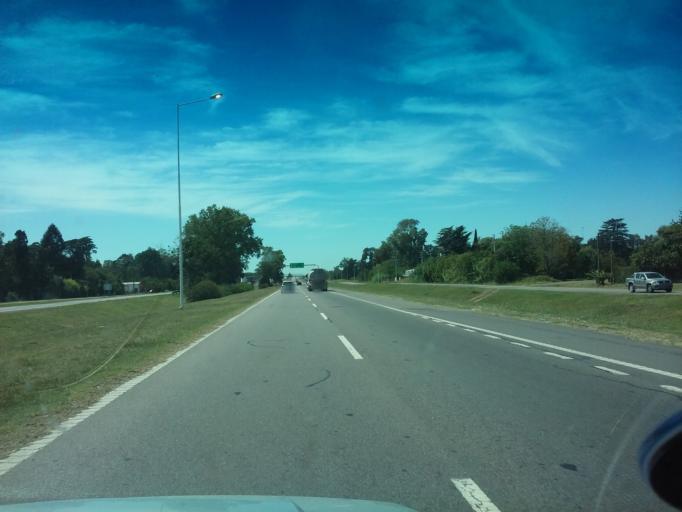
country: AR
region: Buenos Aires
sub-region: Partido de Mercedes
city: Mercedes
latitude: -34.6640
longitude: -59.3952
